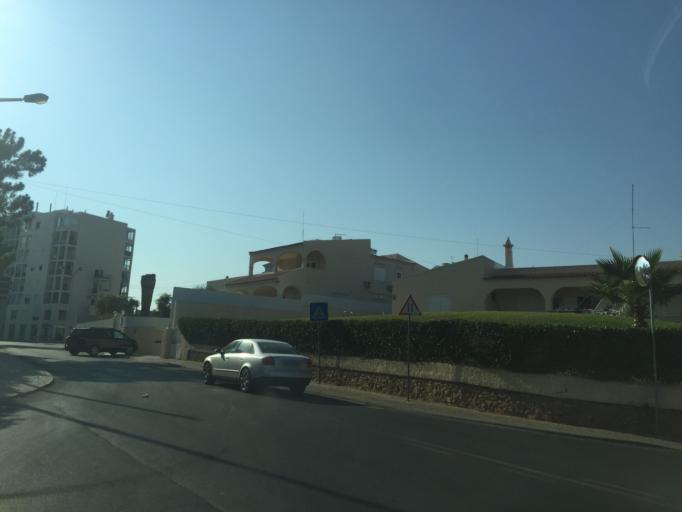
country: PT
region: Faro
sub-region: Loule
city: Quarteira
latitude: 37.0694
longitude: -8.0964
